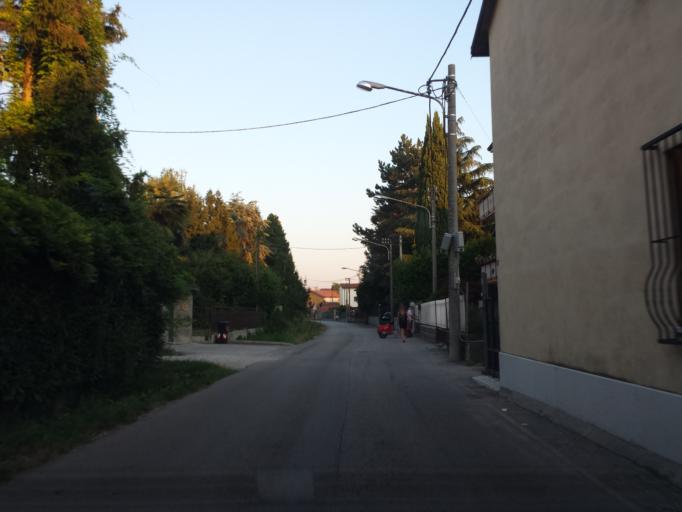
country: IT
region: Veneto
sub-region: Provincia di Vicenza
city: Vicenza
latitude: 45.5683
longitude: 11.5658
